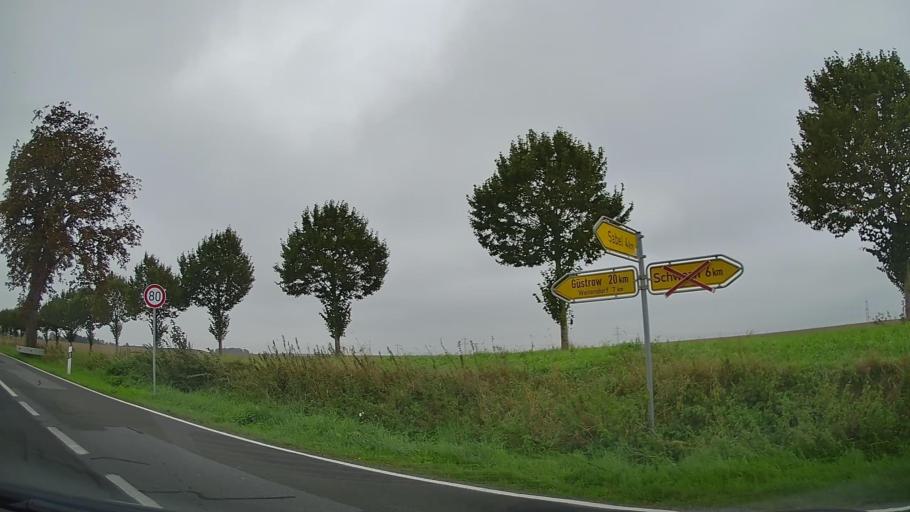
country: DE
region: Mecklenburg-Vorpommern
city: Schwaan
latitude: 53.9190
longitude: 12.1903
